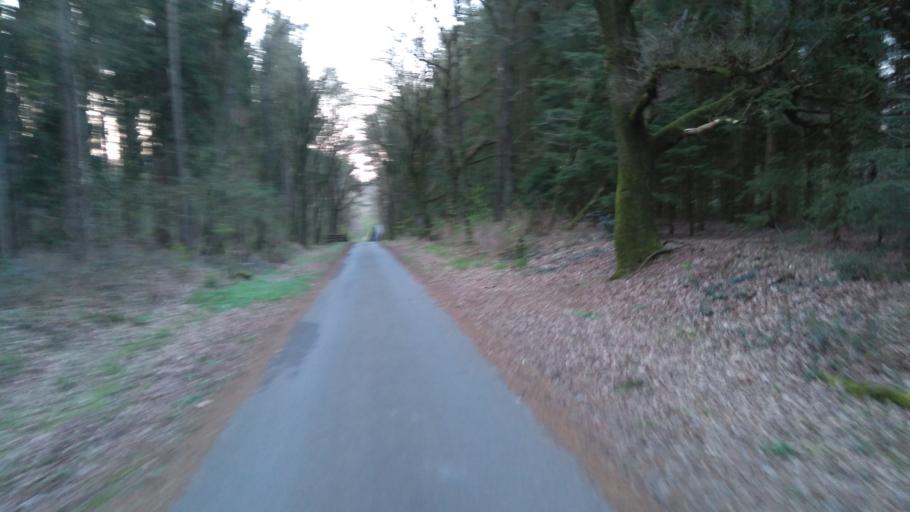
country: DE
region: Lower Saxony
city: Bargstedt
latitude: 53.4532
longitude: 9.4655
